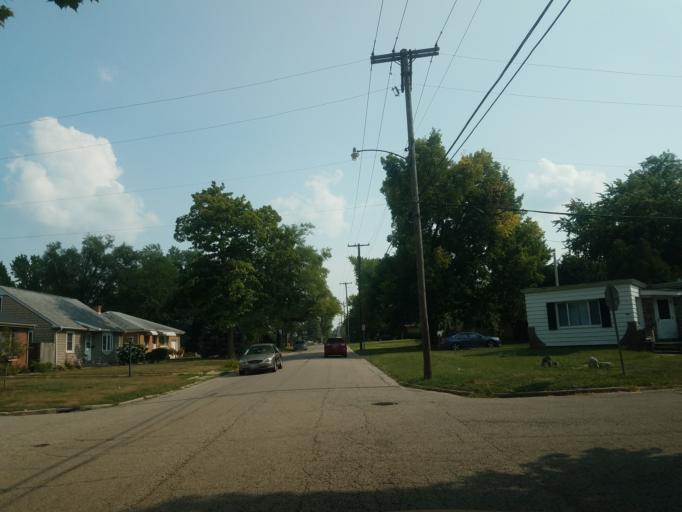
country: US
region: Illinois
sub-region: McLean County
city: Bloomington
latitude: 40.4721
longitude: -88.9724
